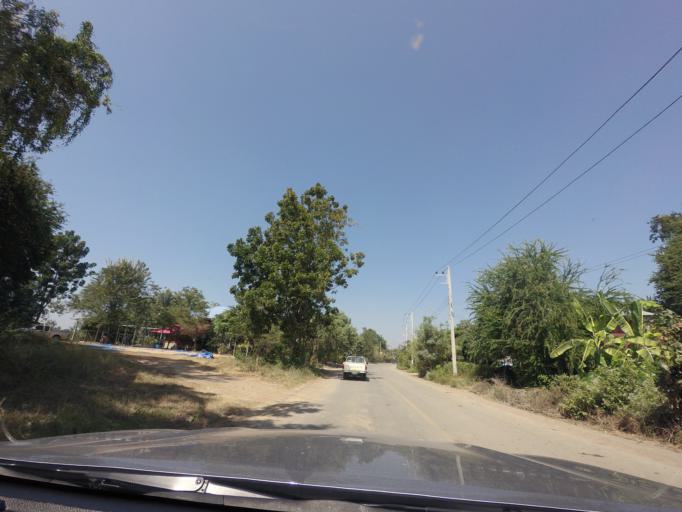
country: TH
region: Sukhothai
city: Si Samrong
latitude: 17.1637
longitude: 99.7703
